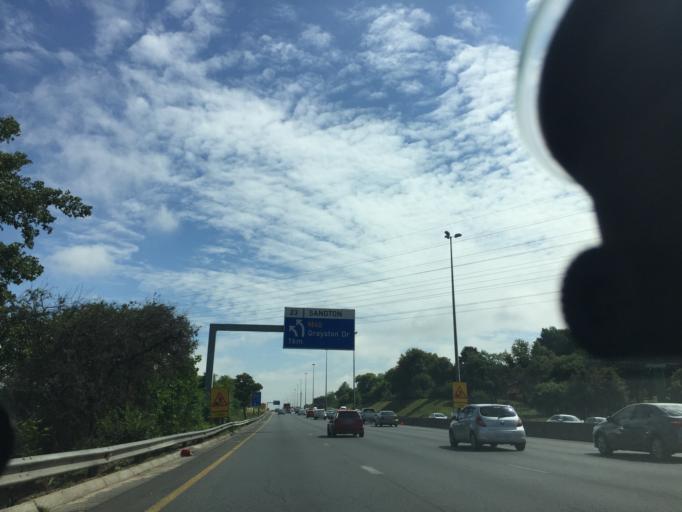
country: ZA
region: Gauteng
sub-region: City of Johannesburg Metropolitan Municipality
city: Johannesburg
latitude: -26.1206
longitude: 28.0728
